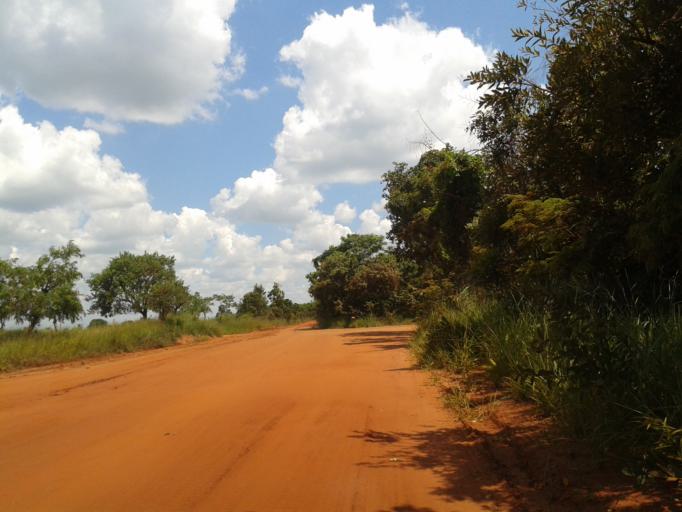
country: BR
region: Minas Gerais
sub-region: Ituiutaba
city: Ituiutaba
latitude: -19.0838
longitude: -49.7319
